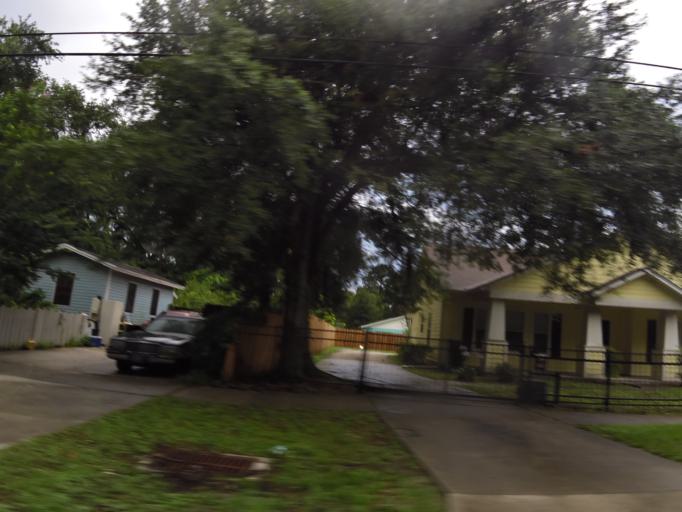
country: US
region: Florida
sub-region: Duval County
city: Jacksonville
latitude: 30.2827
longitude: -81.6385
